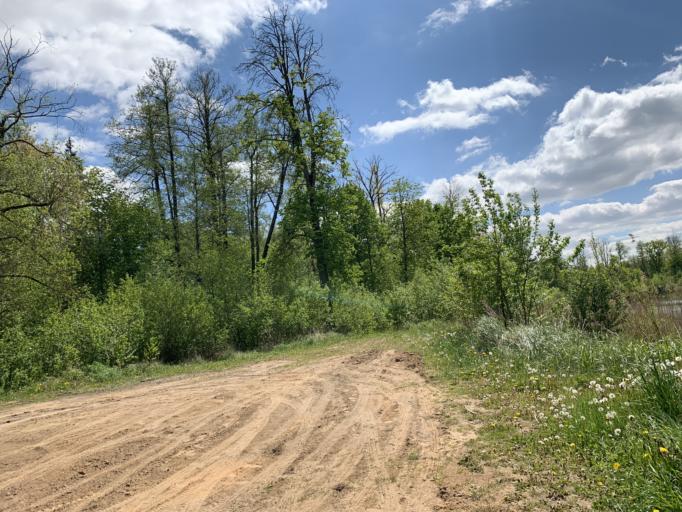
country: BY
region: Minsk
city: Nyasvizh
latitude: 53.1964
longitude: 26.6503
